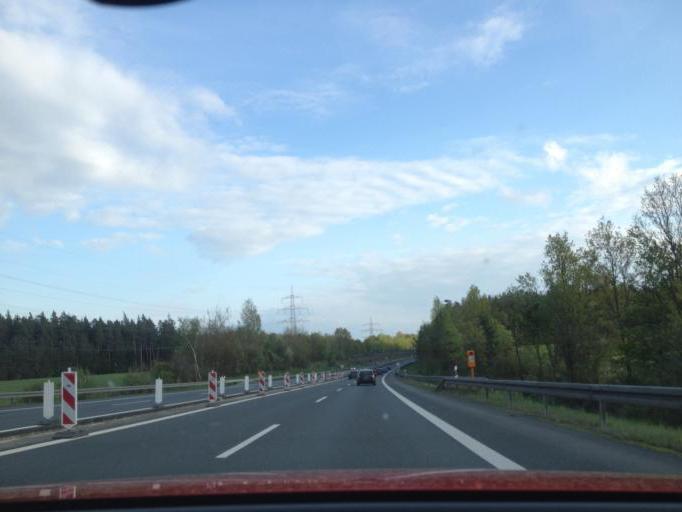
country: DE
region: Bavaria
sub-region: Upper Palatinate
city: Wiesau
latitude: 49.9027
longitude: 12.2210
